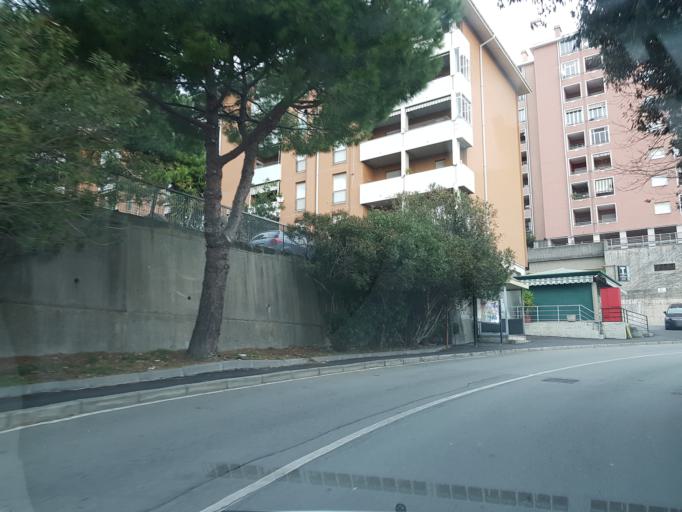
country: IT
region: Liguria
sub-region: Provincia di Genova
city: Mele
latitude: 44.4285
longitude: 8.7977
